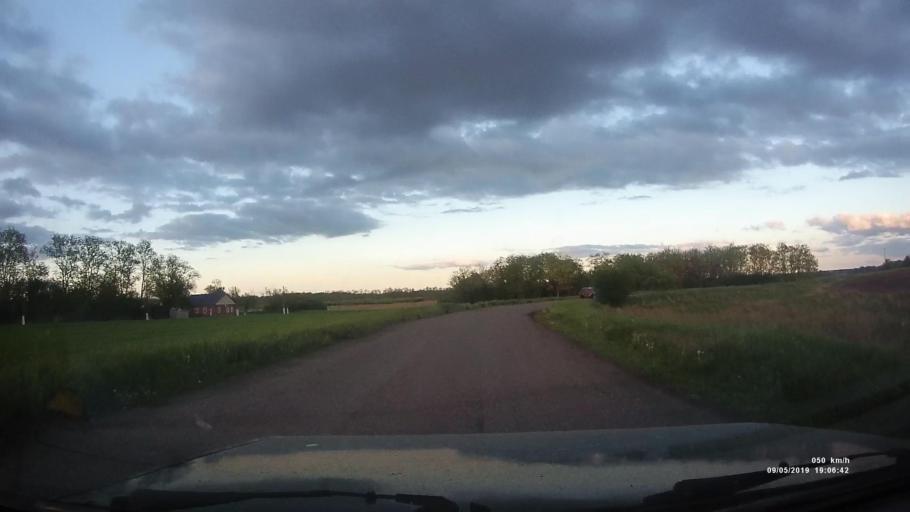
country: RU
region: Krasnodarskiy
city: Kanelovskaya
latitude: 46.7384
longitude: 39.1940
